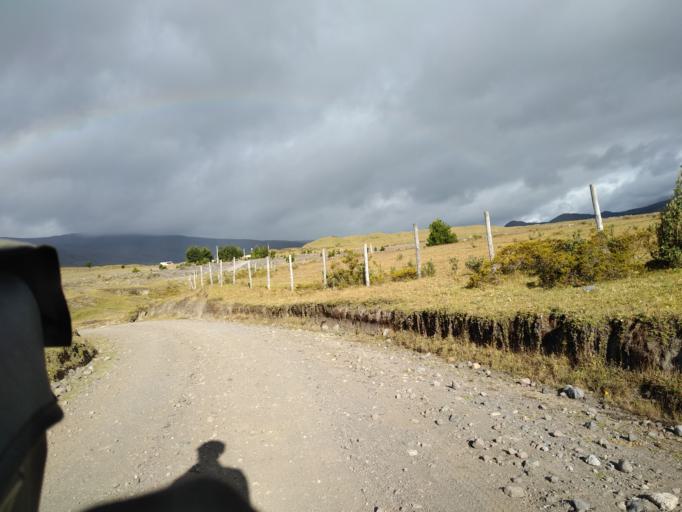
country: EC
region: Pichincha
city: Machachi
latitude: -0.5618
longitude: -78.4474
